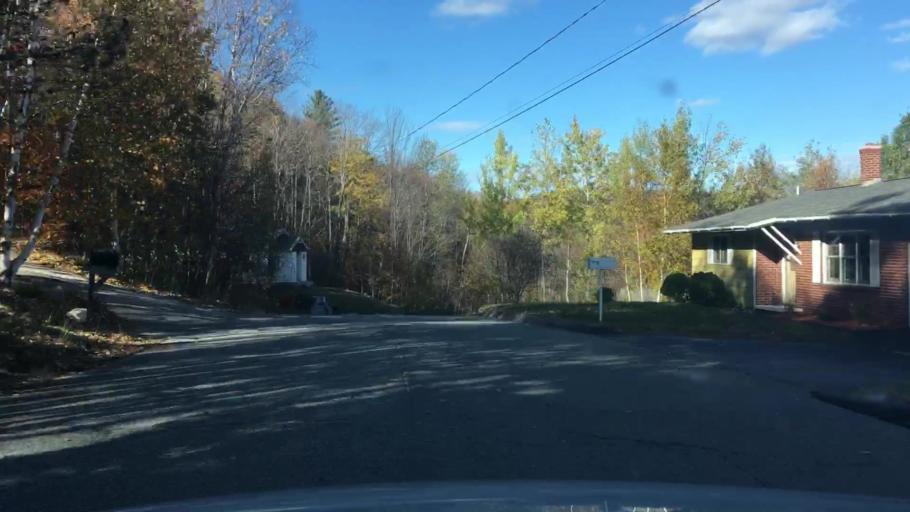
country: US
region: New Hampshire
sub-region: Coos County
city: Berlin
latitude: 44.4691
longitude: -71.1924
